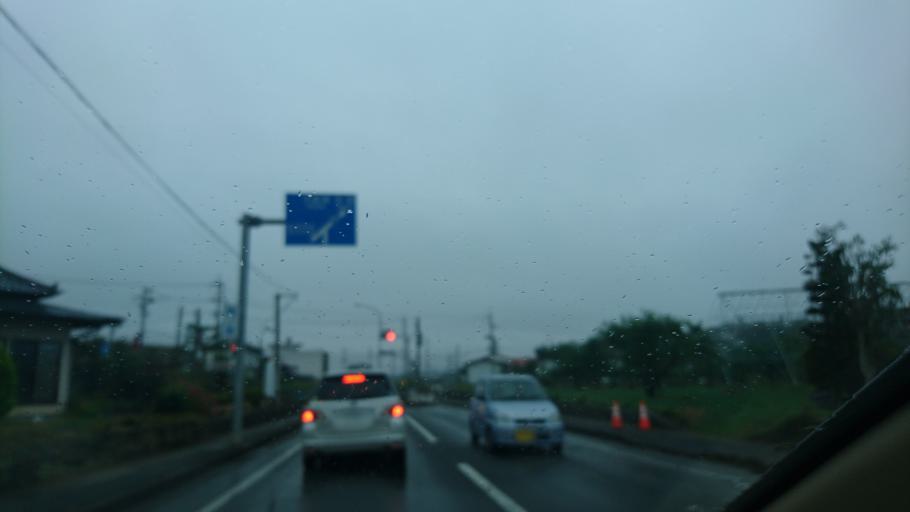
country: JP
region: Iwate
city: Mizusawa
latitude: 39.1356
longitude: 141.1645
